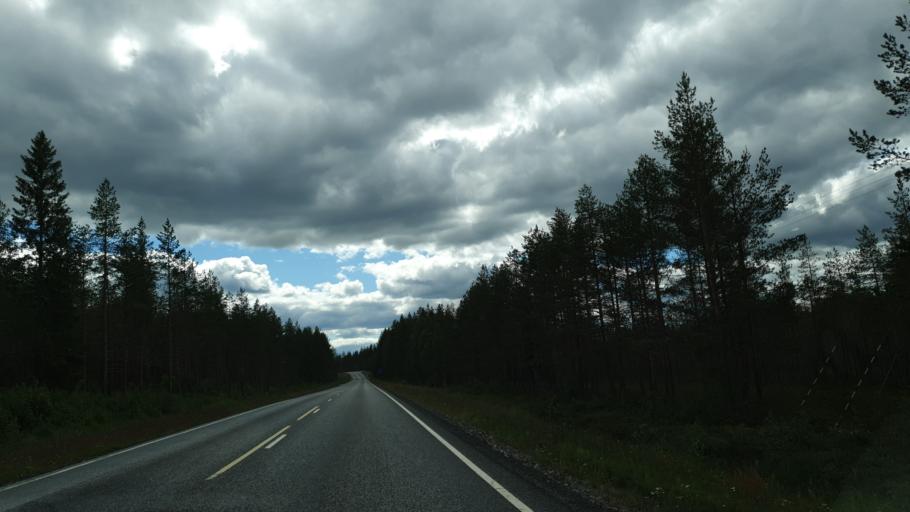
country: FI
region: Kainuu
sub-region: Kehys-Kainuu
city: Kuhmo
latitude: 64.0387
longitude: 29.5745
